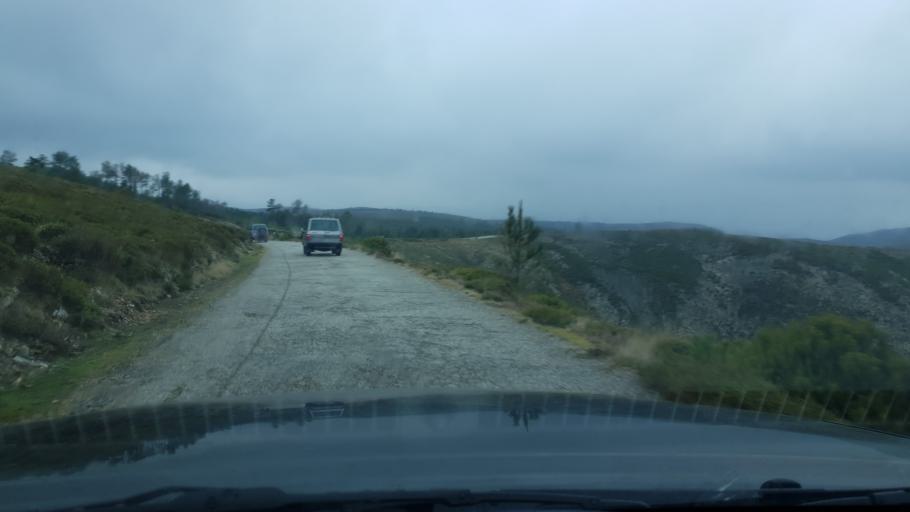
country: PT
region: Viseu
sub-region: Sao Pedro do Sul
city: Sao Pedro do Sul
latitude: 40.8704
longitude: -8.0804
